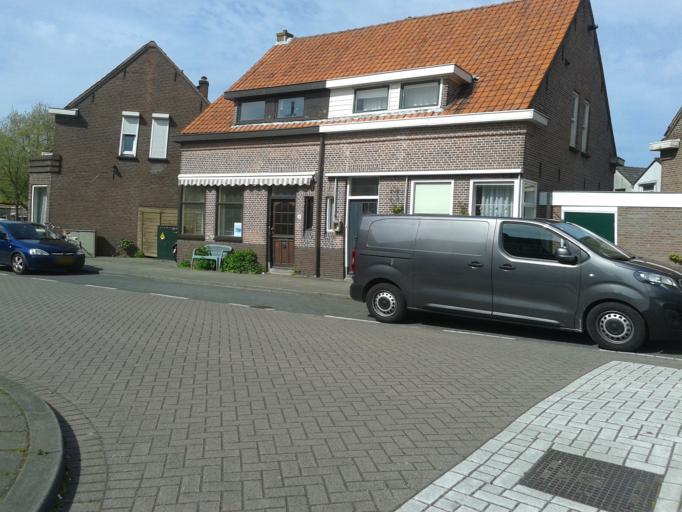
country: NL
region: South Holland
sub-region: Gemeente Gouda
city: Gouda
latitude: 52.0121
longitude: 4.7199
